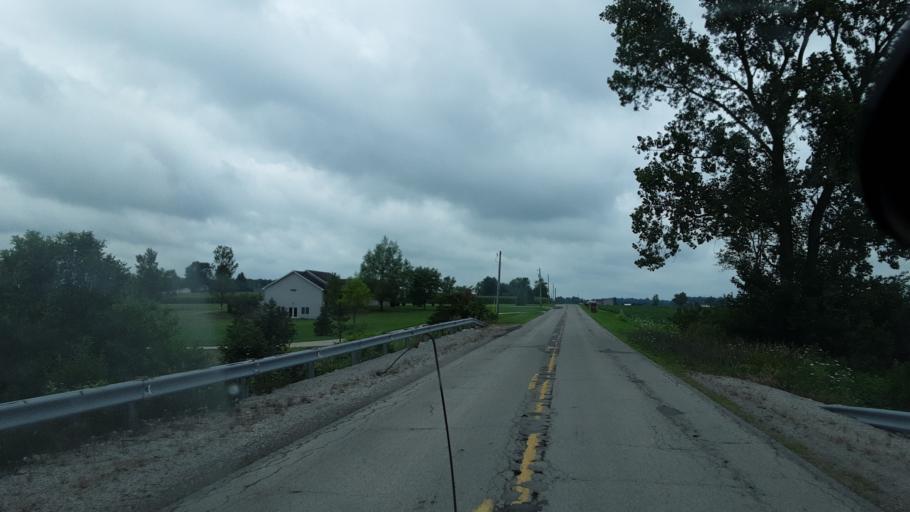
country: US
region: Indiana
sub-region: Wells County
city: Ossian
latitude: 40.9322
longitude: -85.1045
